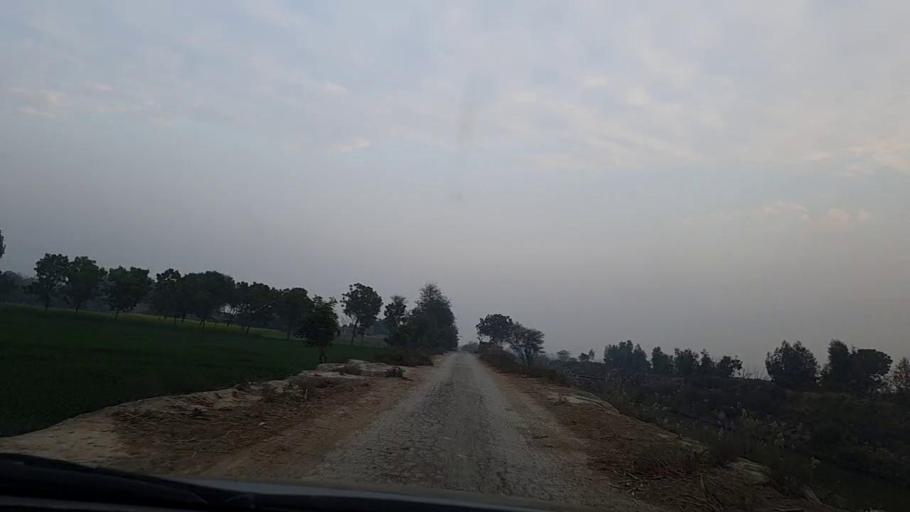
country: PK
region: Sindh
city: Sakrand
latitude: 26.2879
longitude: 68.2382
